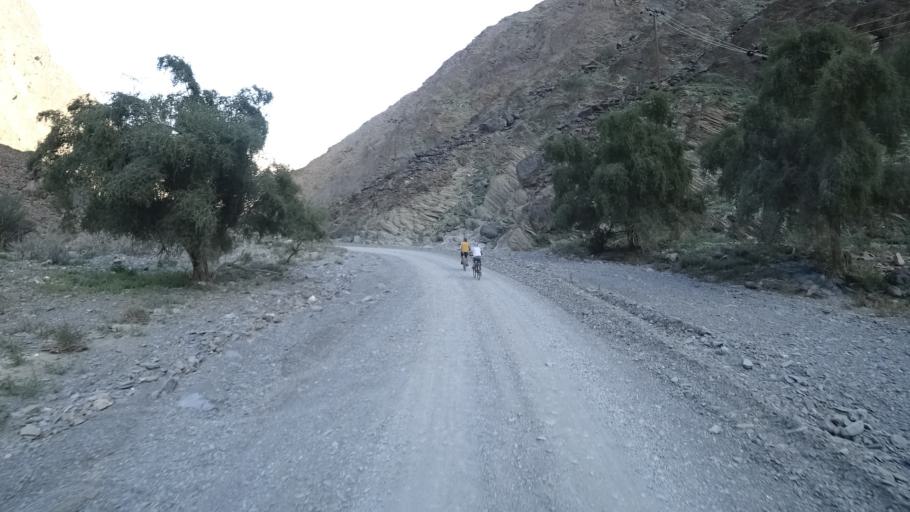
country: OM
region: Al Batinah
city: Bayt al `Awabi
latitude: 23.2538
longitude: 57.3978
